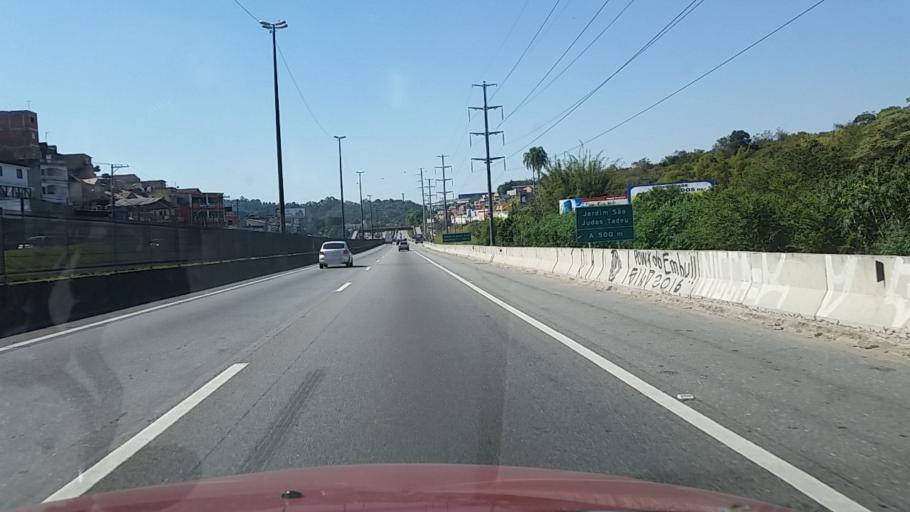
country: BR
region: Sao Paulo
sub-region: Taboao Da Serra
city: Taboao da Serra
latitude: -23.6292
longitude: -46.8196
